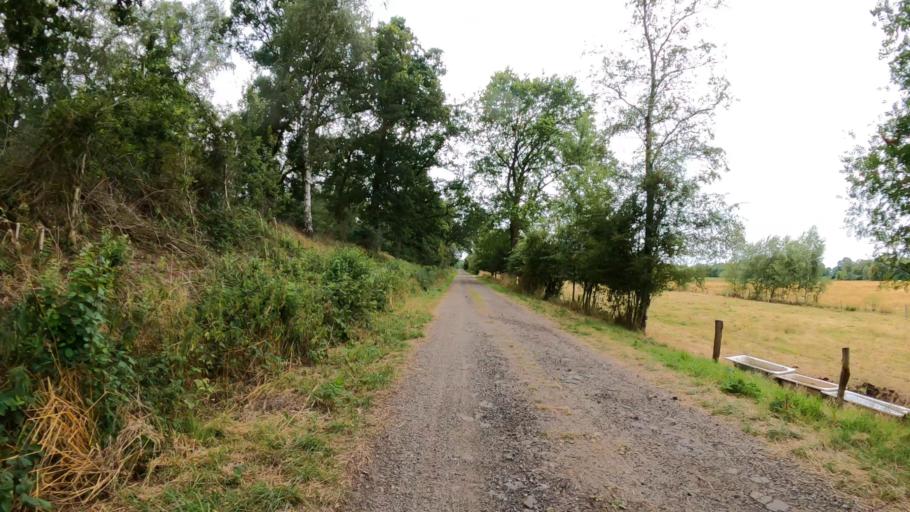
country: DE
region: Schleswig-Holstein
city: Seth
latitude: 53.8483
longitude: 10.1935
